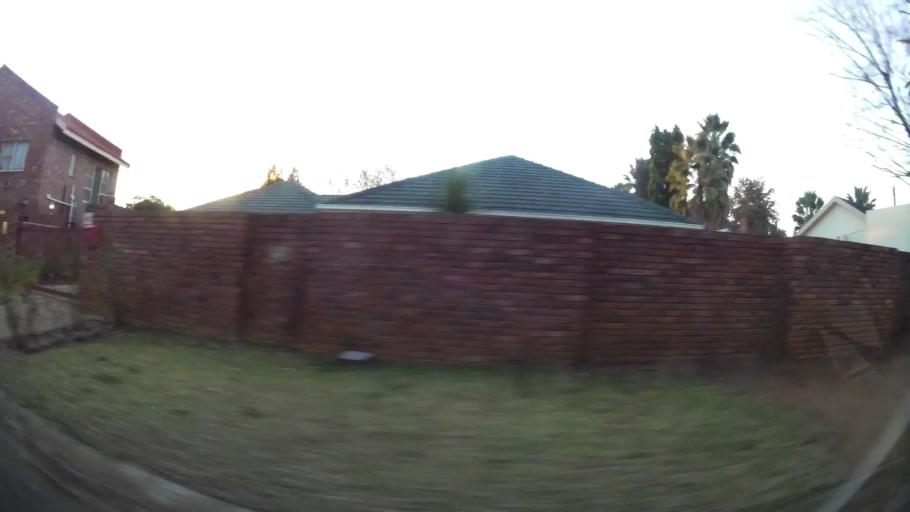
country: ZA
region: North-West
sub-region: Dr Kenneth Kaunda District Municipality
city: Potchefstroom
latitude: -26.7253
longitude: 27.1091
